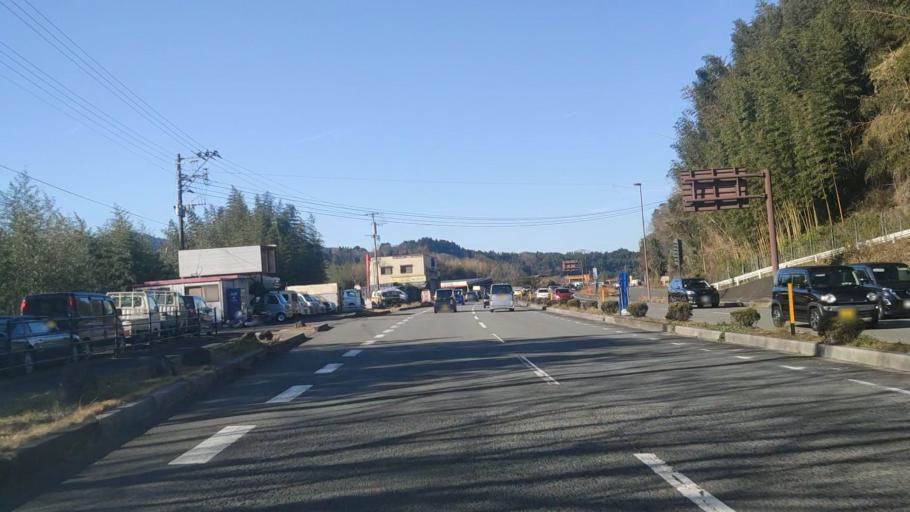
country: JP
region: Oita
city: Oita
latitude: 33.1138
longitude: 131.6552
